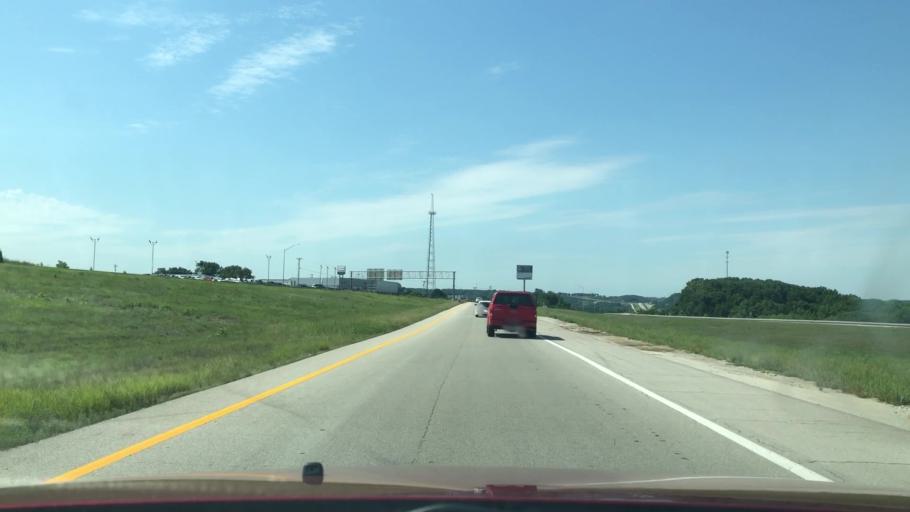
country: US
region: Missouri
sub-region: Taney County
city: Merriam Woods
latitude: 36.7119
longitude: -93.2198
